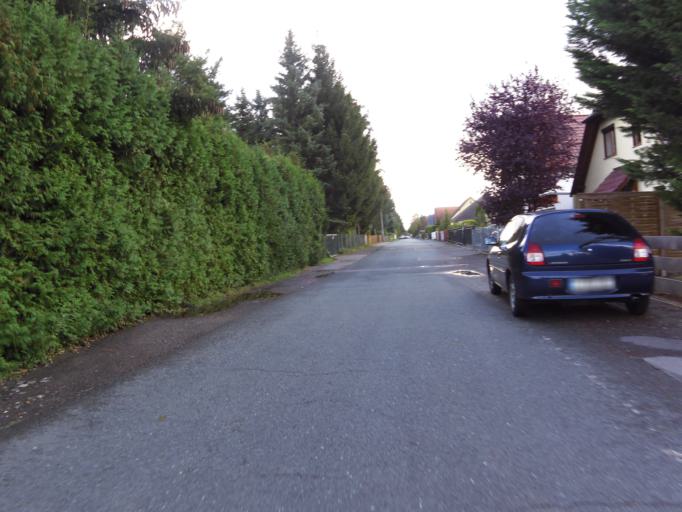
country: DE
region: Saxony
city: Taucha
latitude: 51.3235
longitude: 12.4757
